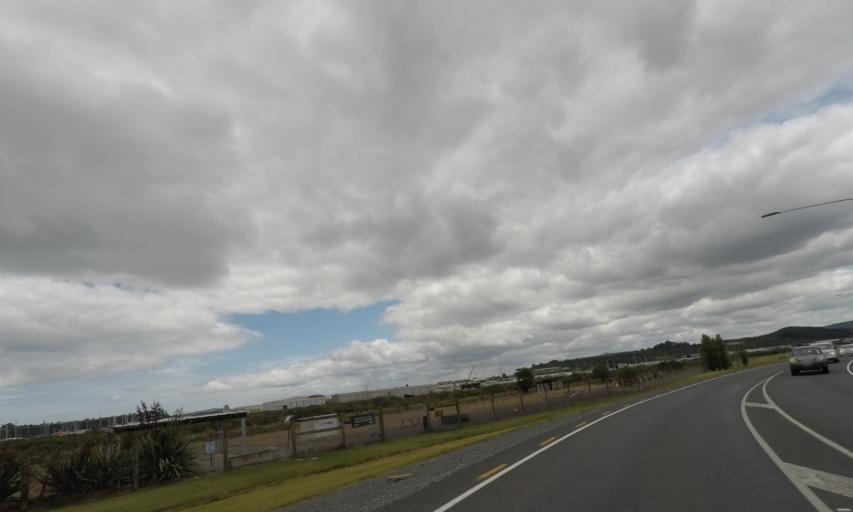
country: NZ
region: Northland
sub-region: Whangarei
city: Whangarei
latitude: -35.7336
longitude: 174.3428
